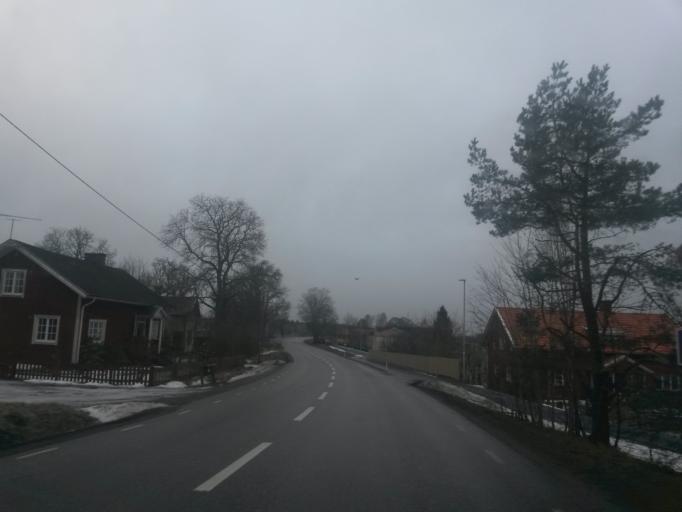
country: SE
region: Vaestra Goetaland
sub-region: Alingsas Kommun
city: Sollebrunn
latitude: 58.1125
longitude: 12.6201
